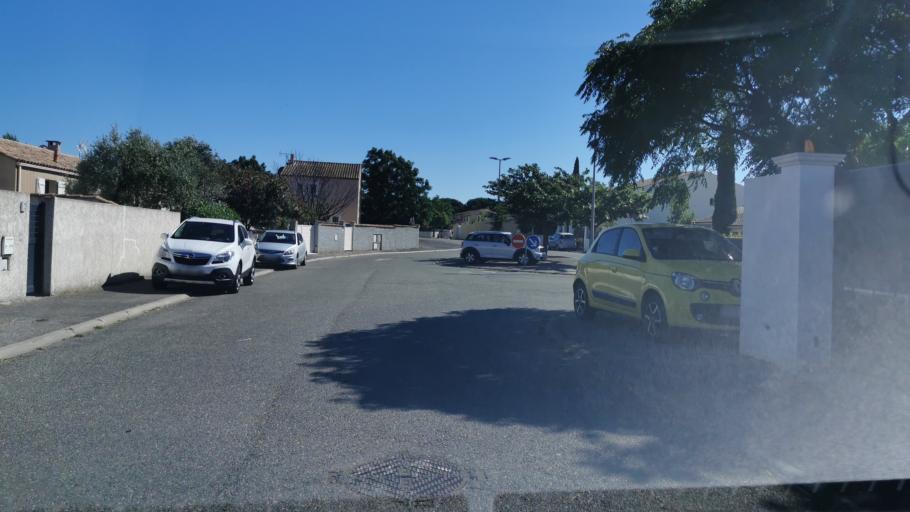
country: FR
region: Languedoc-Roussillon
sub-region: Departement de l'Aude
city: Narbonne
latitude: 43.1984
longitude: 3.0175
